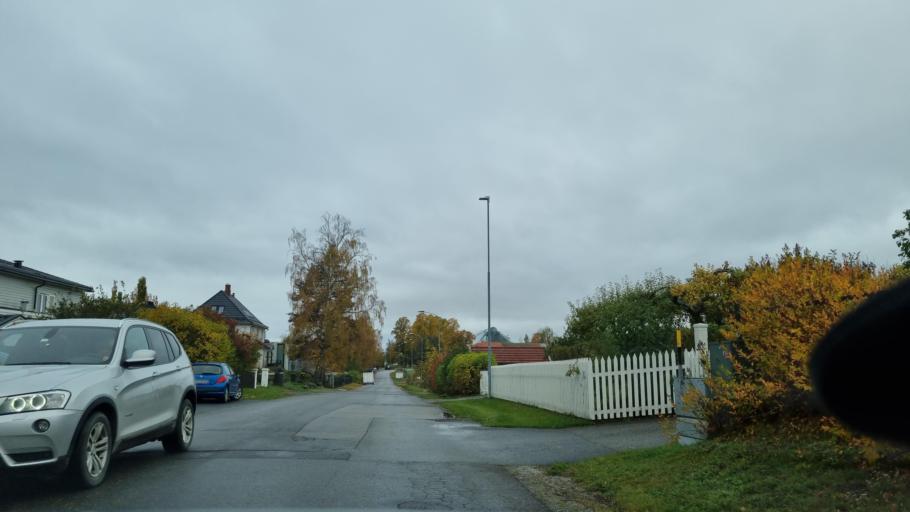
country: NO
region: Hedmark
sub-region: Hamar
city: Hamar
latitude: 60.7930
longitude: 11.0471
